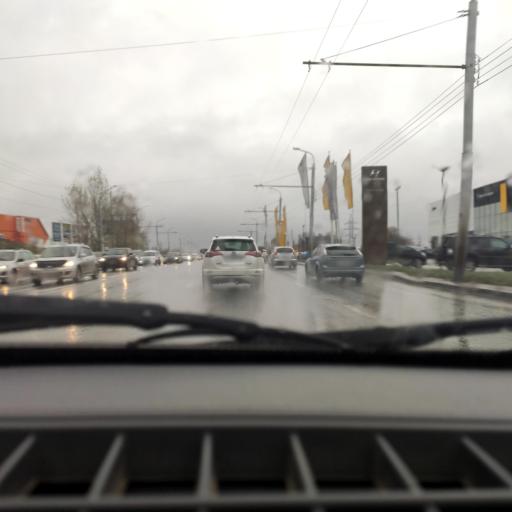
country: RU
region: Bashkortostan
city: Ufa
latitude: 54.7835
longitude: 56.0745
